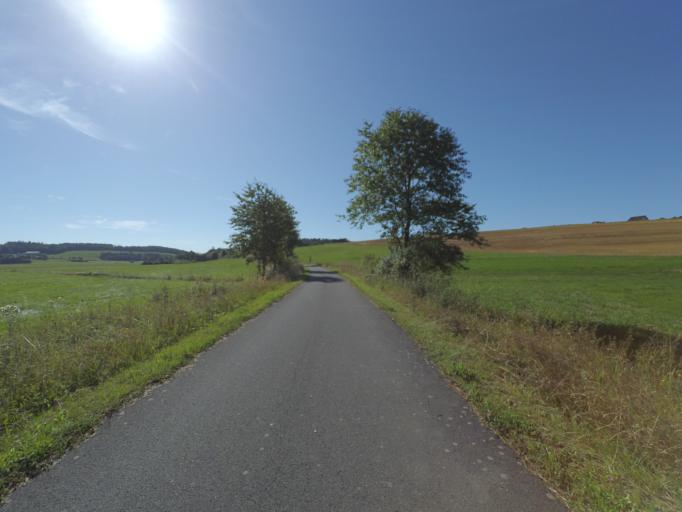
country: DE
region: Rheinland-Pfalz
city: Udler
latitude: 50.1418
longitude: 6.8803
